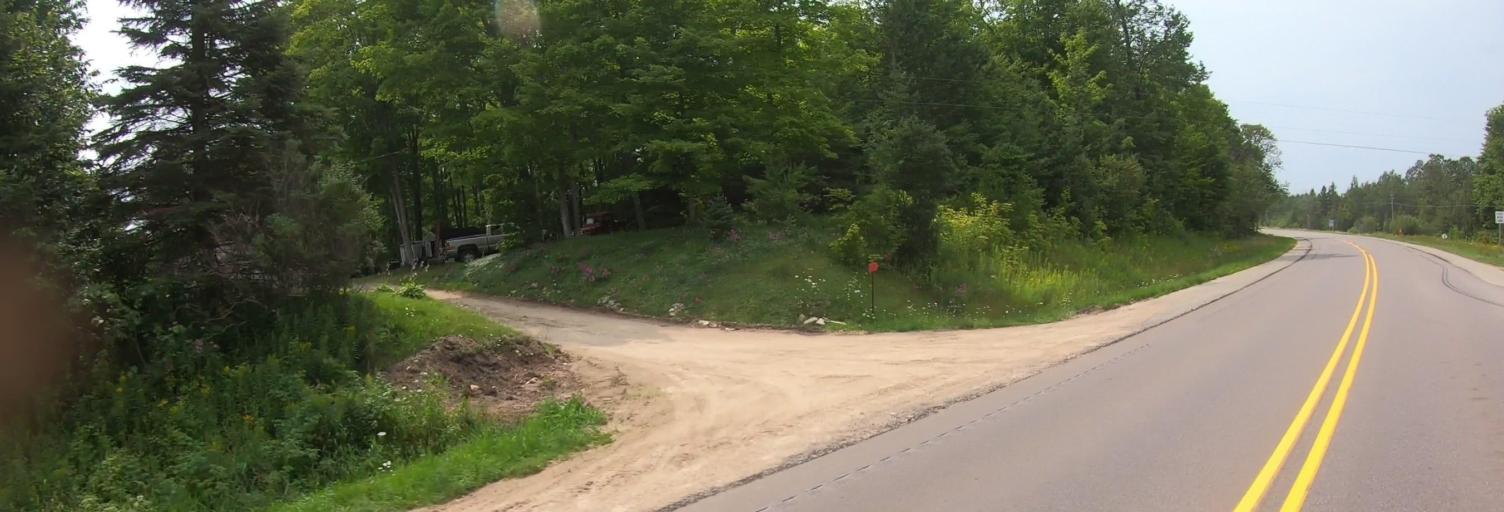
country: US
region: Michigan
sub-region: Alger County
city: Munising
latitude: 46.3545
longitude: -86.9586
